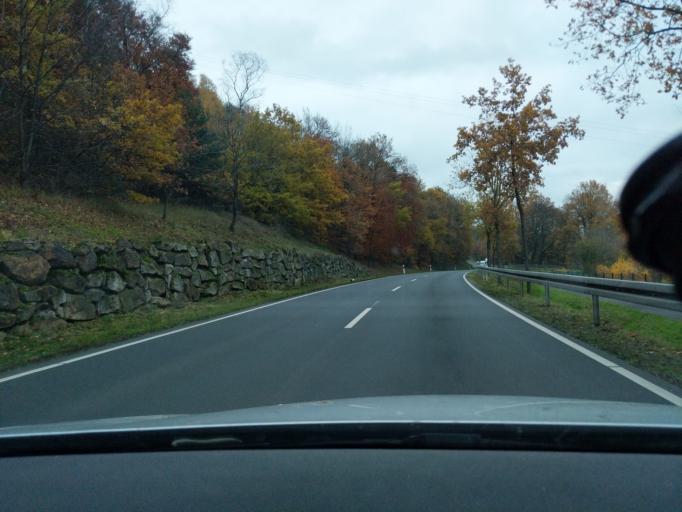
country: DE
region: North Rhine-Westphalia
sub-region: Regierungsbezirk Munster
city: Horstel
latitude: 52.2751
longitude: 7.6118
